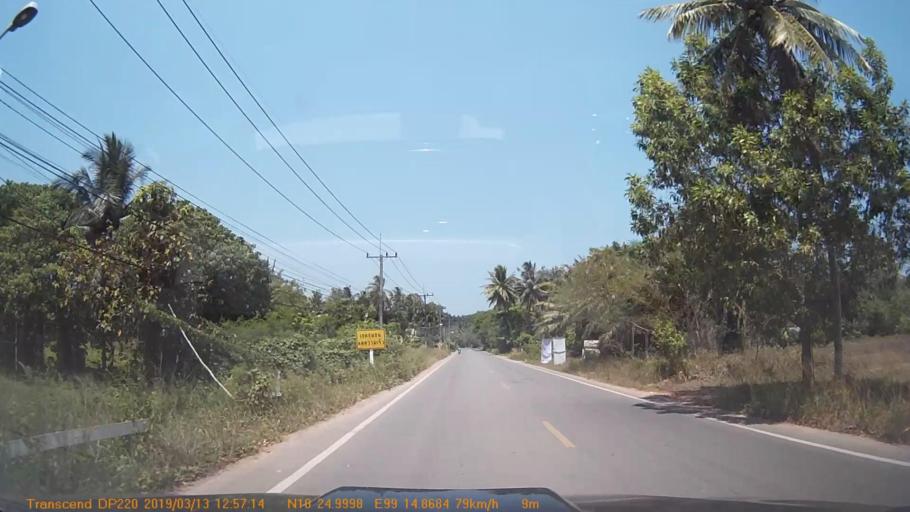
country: TH
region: Chumphon
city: Chumphon
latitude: 10.4172
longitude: 99.2479
